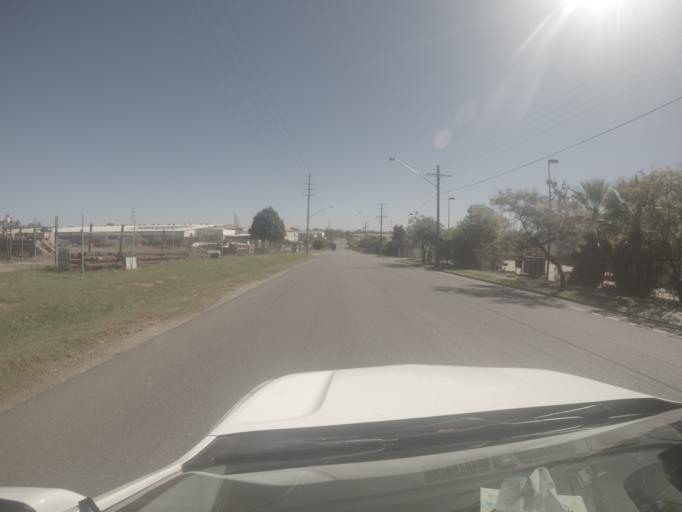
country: AU
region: Queensland
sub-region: Brisbane
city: Richlands
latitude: -27.5788
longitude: 152.9543
